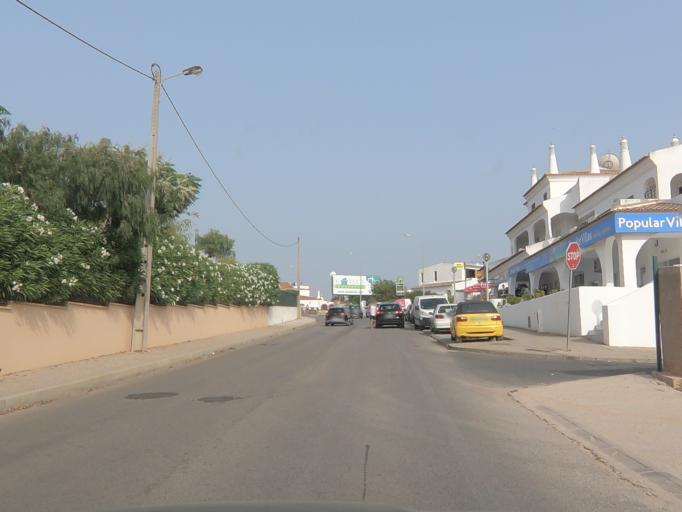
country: PT
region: Faro
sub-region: Albufeira
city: Guia
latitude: 37.0796
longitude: -8.3007
